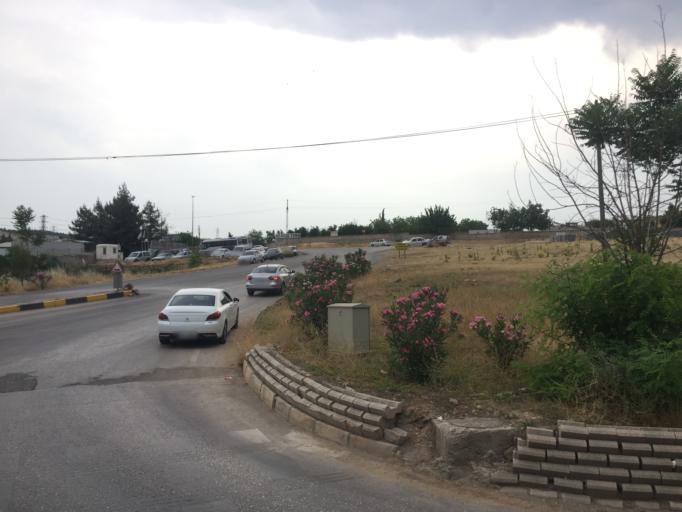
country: TR
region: Gaziantep
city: Gaziantep
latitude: 37.0220
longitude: 37.4284
